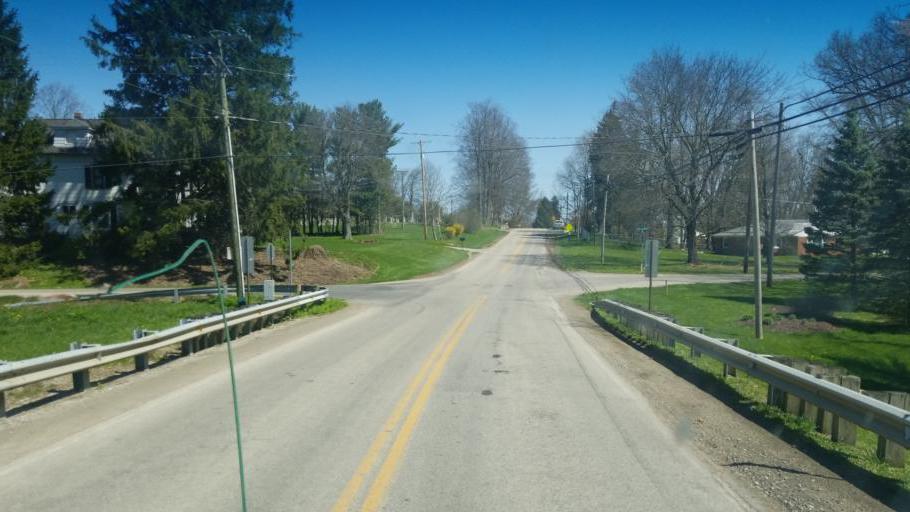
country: US
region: Ohio
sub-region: Richland County
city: Lincoln Heights
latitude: 40.8004
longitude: -82.4438
